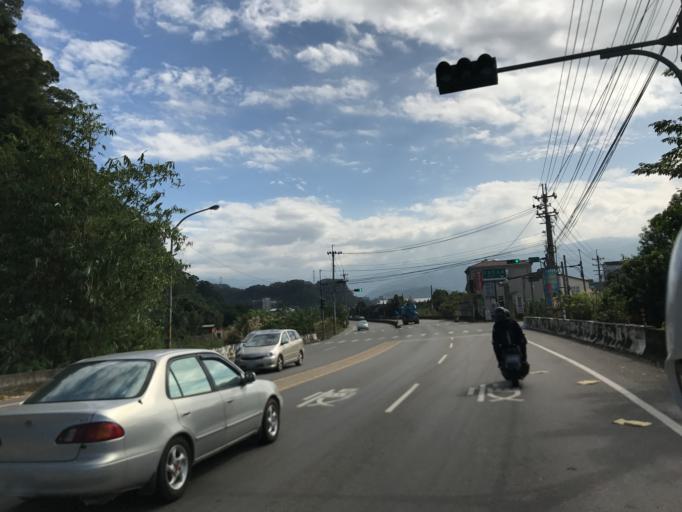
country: TW
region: Taiwan
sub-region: Hsinchu
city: Zhubei
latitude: 24.7387
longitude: 121.1118
